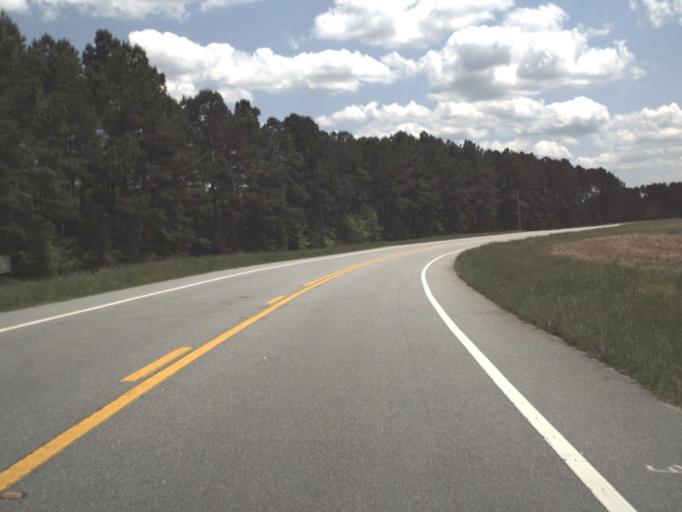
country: US
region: Florida
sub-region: Escambia County
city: Molino
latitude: 30.8463
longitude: -87.4356
